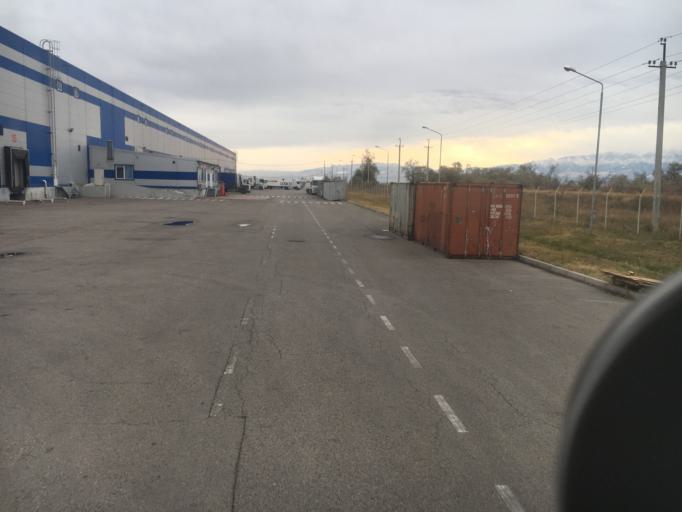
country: KZ
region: Almaty Oblysy
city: Energeticheskiy
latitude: 43.5835
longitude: 77.0939
